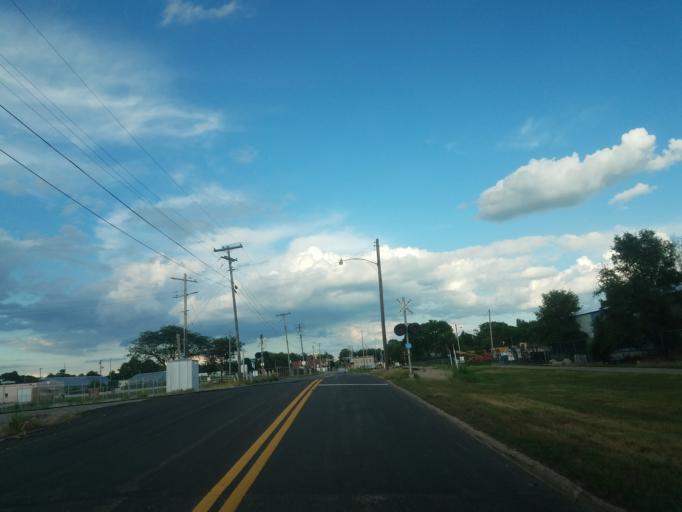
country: US
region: Illinois
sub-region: McLean County
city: Bloomington
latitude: 40.4792
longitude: -89.0118
